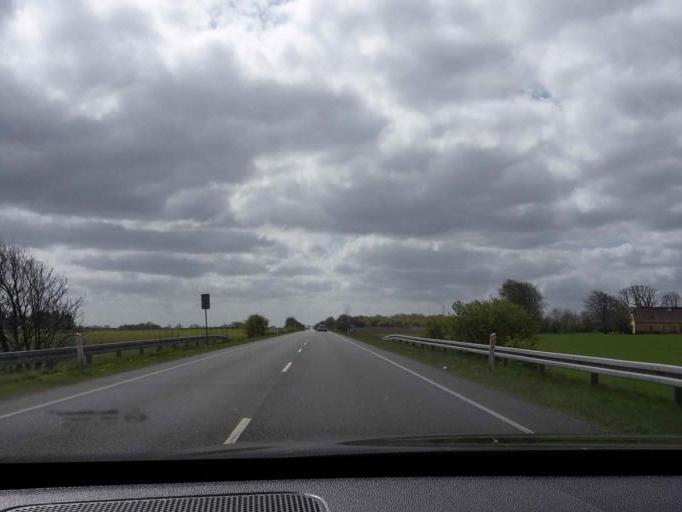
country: DK
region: South Denmark
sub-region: Varde Kommune
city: Olgod
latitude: 55.7696
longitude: 8.6219
